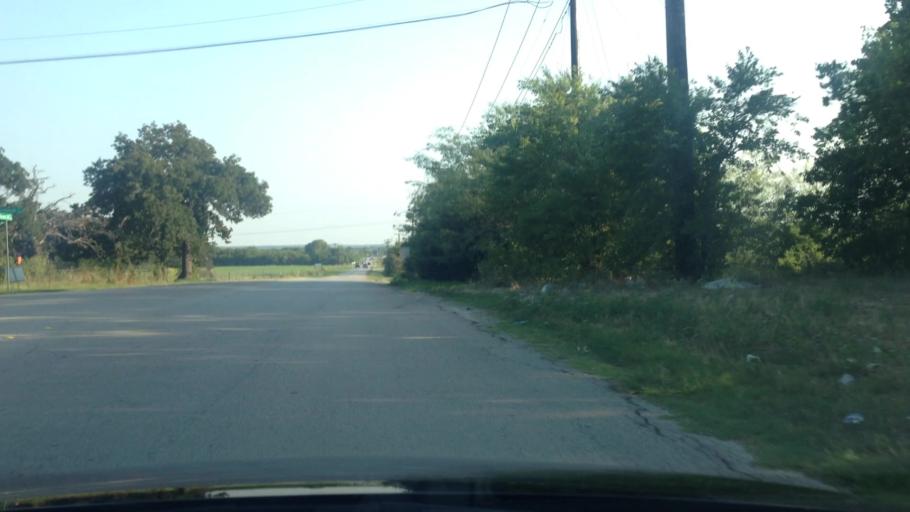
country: US
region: Texas
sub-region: Tarrant County
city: Everman
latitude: 32.6458
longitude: -97.2700
